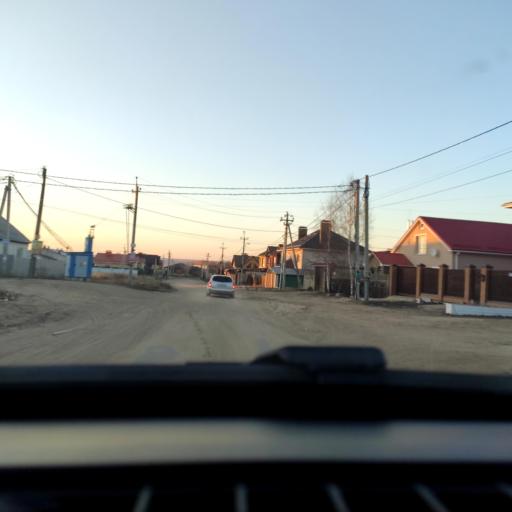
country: RU
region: Voronezj
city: Podgornoye
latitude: 51.7250
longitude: 39.1370
